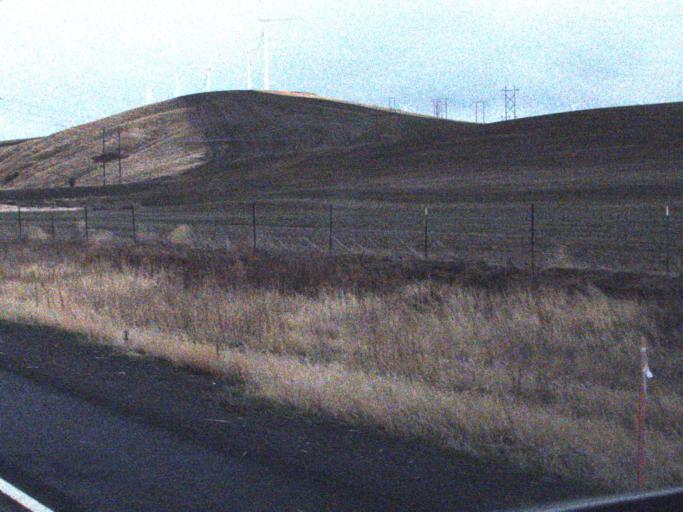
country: US
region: Washington
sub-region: Columbia County
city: Dayton
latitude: 46.5363
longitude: -117.8547
